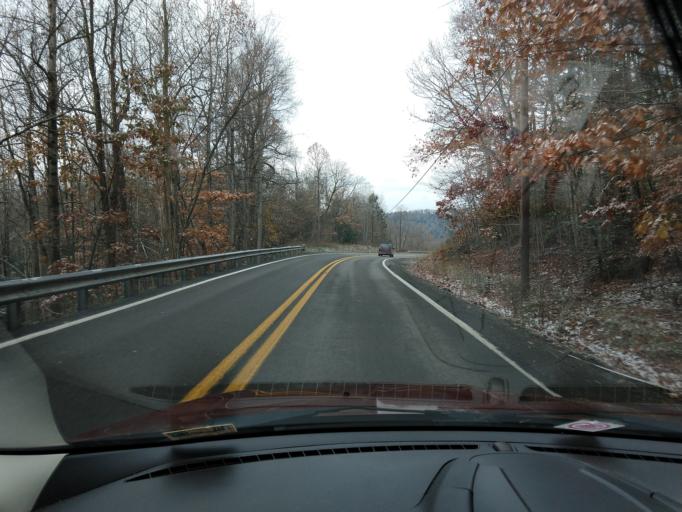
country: US
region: West Virginia
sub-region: Nicholas County
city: Craigsville
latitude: 38.2469
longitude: -80.7191
